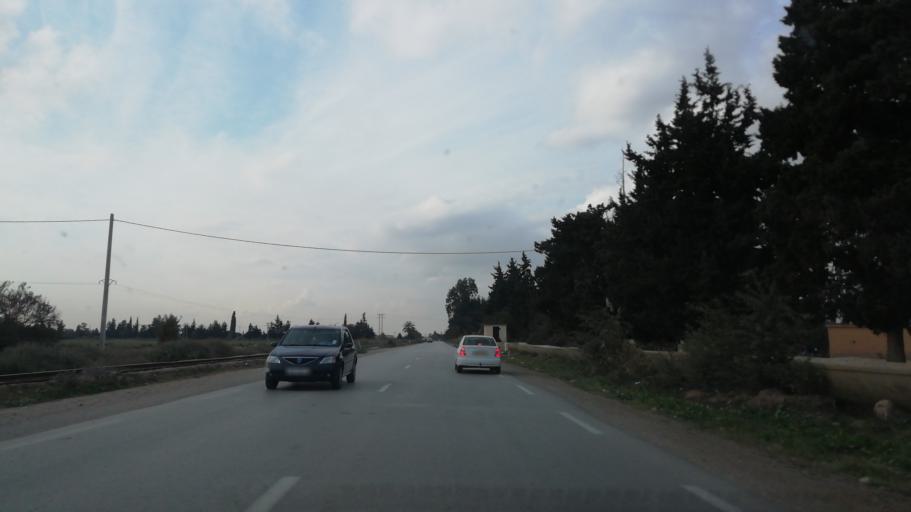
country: DZ
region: Mascara
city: Sig
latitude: 35.6629
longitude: 0.0053
